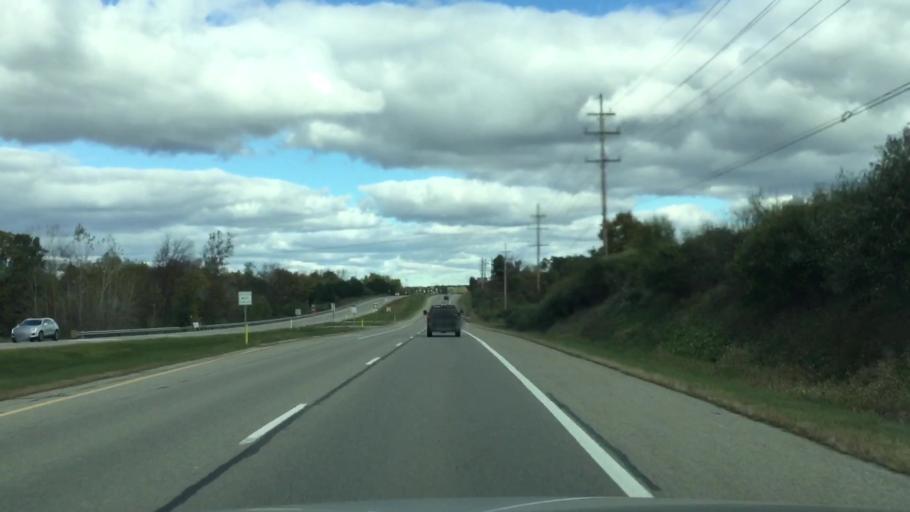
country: US
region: Michigan
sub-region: Lapeer County
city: Lapeer
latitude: 42.9642
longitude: -83.3142
